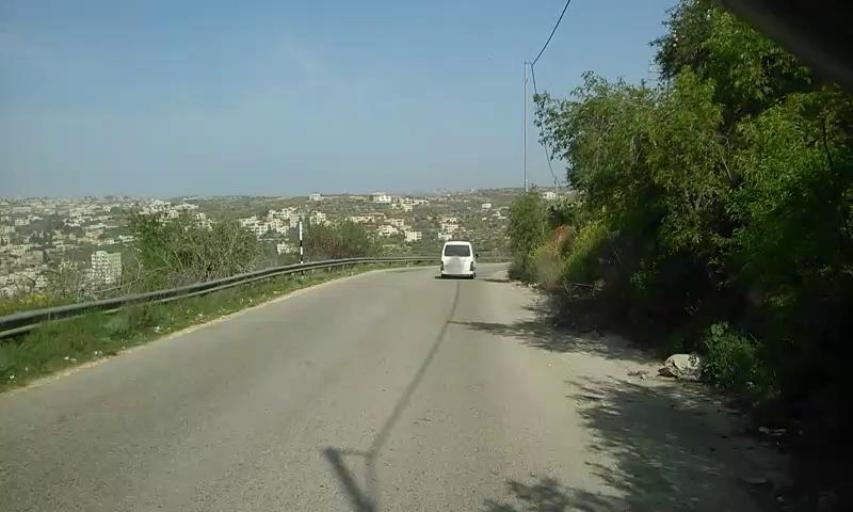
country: PS
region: West Bank
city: Dura al Qar`
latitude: 31.9594
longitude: 35.2248
